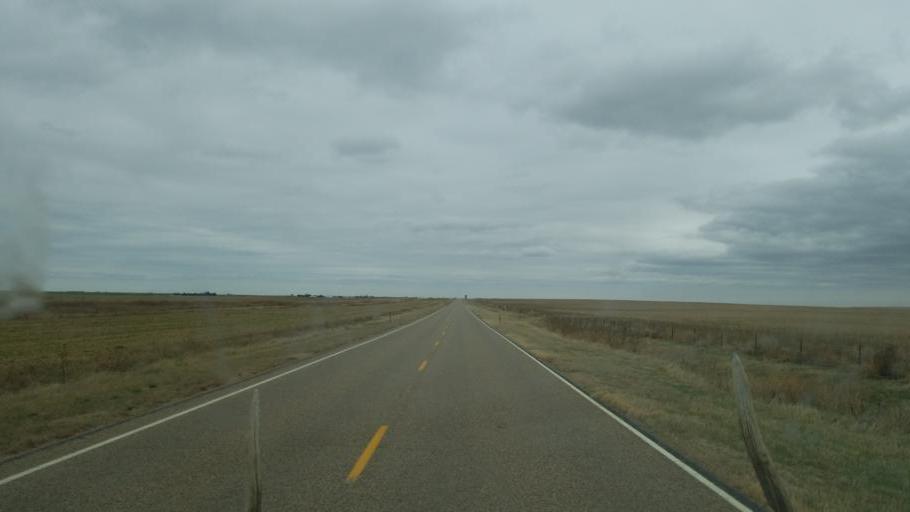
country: US
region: Colorado
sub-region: Cheyenne County
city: Cheyenne Wells
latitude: 38.8529
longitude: -102.2136
